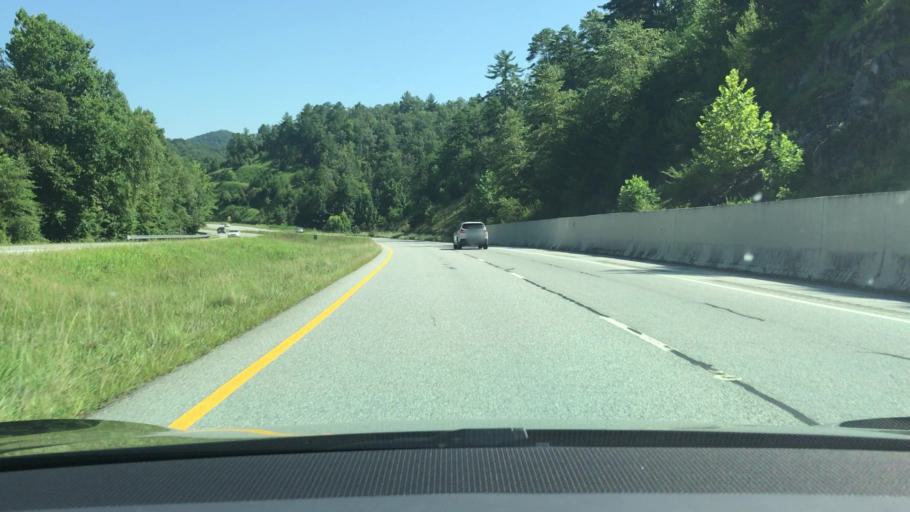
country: US
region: Georgia
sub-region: Rabun County
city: Clayton
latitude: 34.7712
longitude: -83.3954
